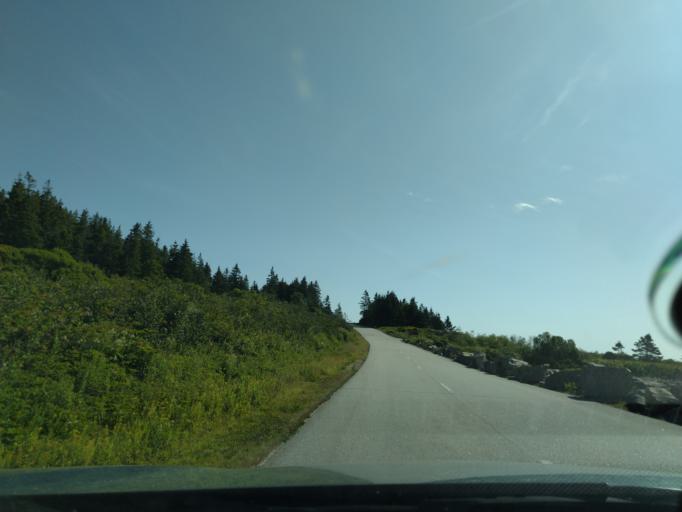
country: US
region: Maine
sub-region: Hancock County
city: Gouldsboro
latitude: 44.3385
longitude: -68.0476
